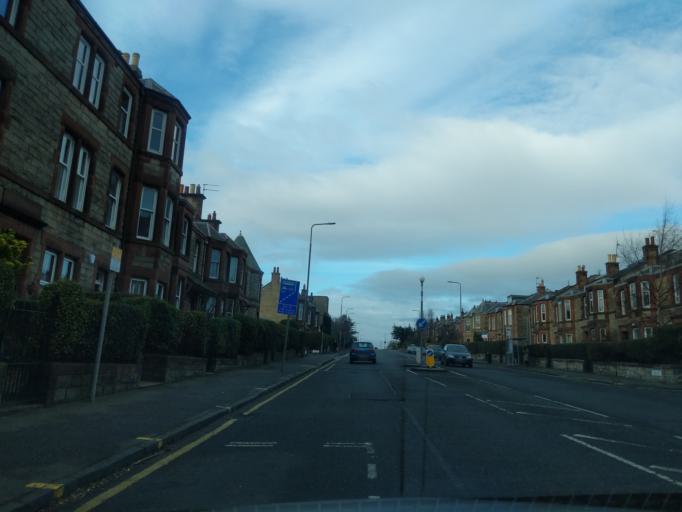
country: GB
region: Scotland
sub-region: Edinburgh
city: Colinton
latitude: 55.9577
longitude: -3.2504
